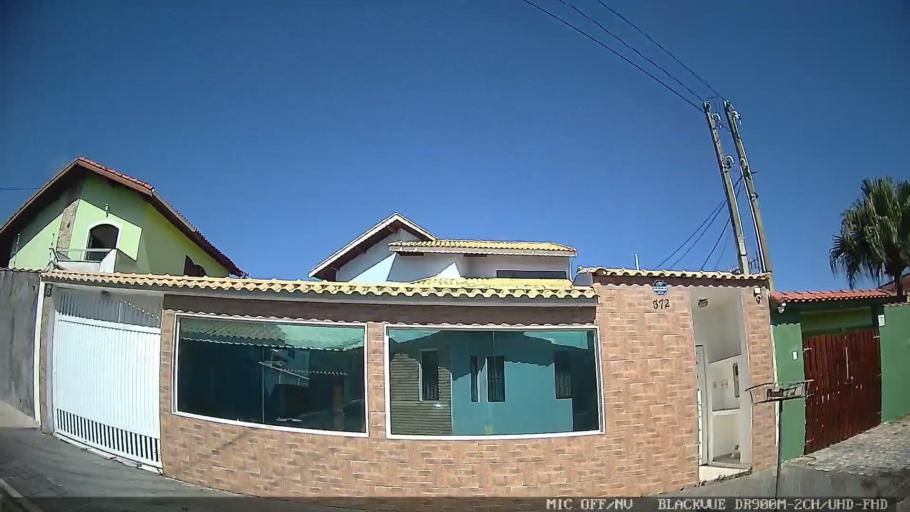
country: BR
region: Sao Paulo
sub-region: Peruibe
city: Peruibe
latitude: -24.3072
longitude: -46.9923
